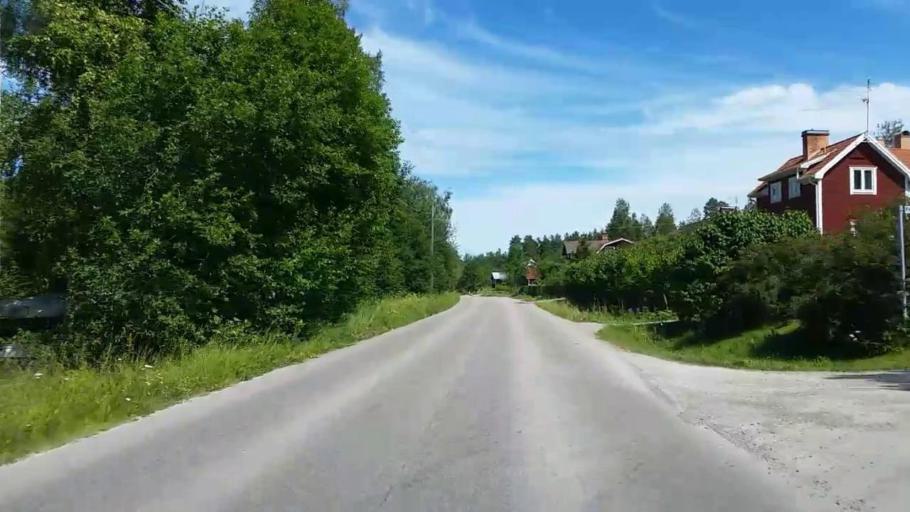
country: SE
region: Dalarna
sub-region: Rattviks Kommun
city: Raettvik
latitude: 60.8861
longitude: 15.1351
